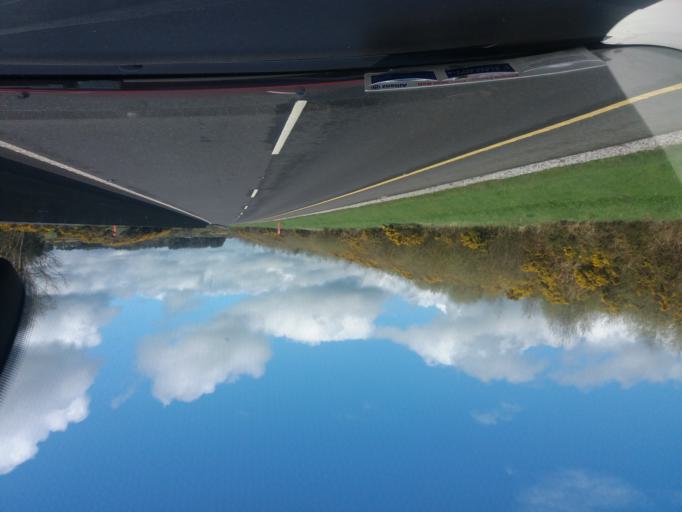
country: IE
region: Munster
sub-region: County Cork
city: Fermoy
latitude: 52.2010
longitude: -8.2741
